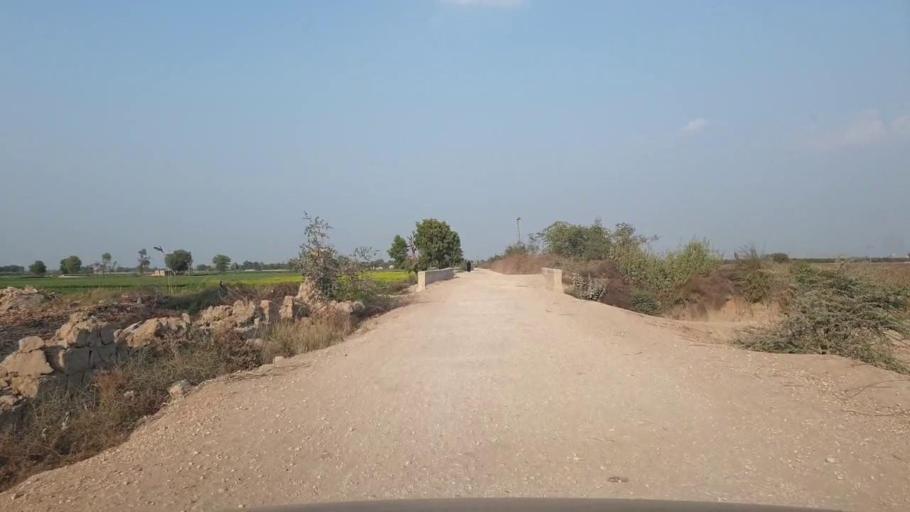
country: PK
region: Sindh
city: Bhit Shah
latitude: 25.7939
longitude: 68.4578
